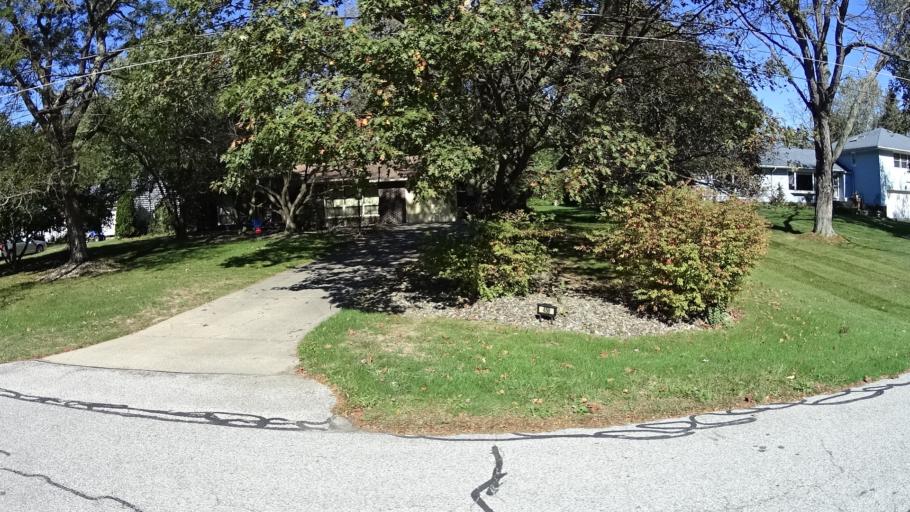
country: US
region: Ohio
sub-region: Lorain County
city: Oberlin
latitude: 41.2902
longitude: -82.2004
